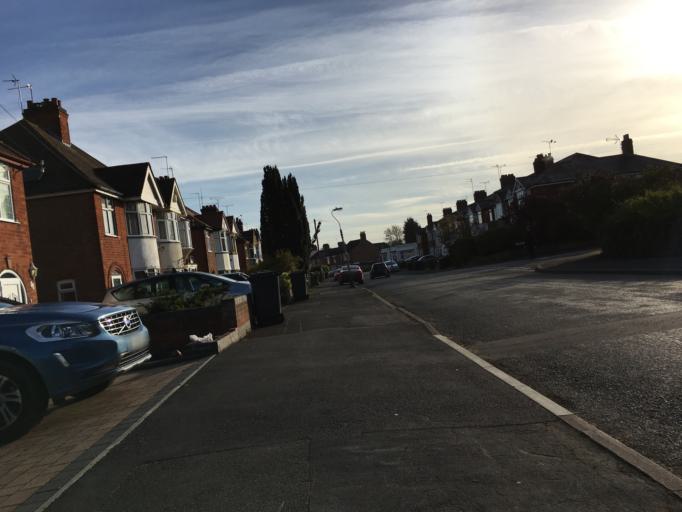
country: GB
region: England
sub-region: Warwickshire
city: Rugby
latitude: 52.3649
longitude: -1.2519
